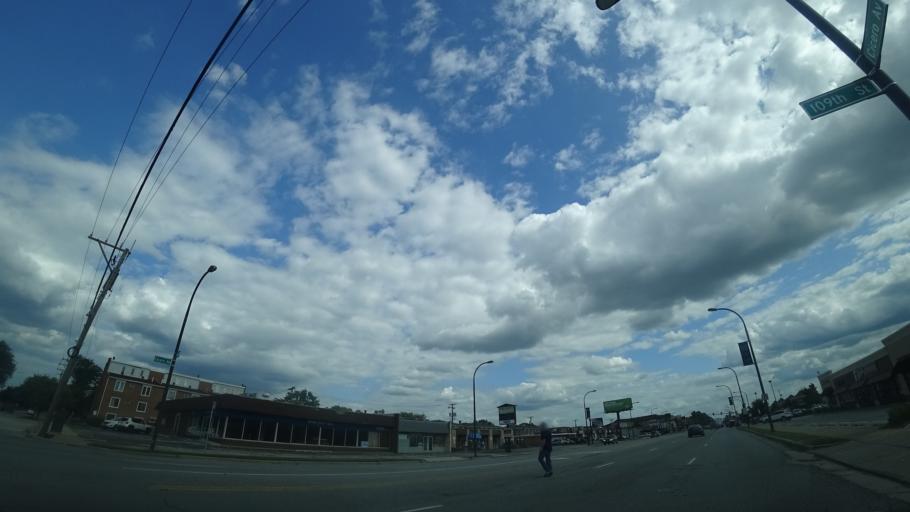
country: US
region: Illinois
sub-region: Cook County
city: Oak Lawn
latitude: 41.6945
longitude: -87.7400
